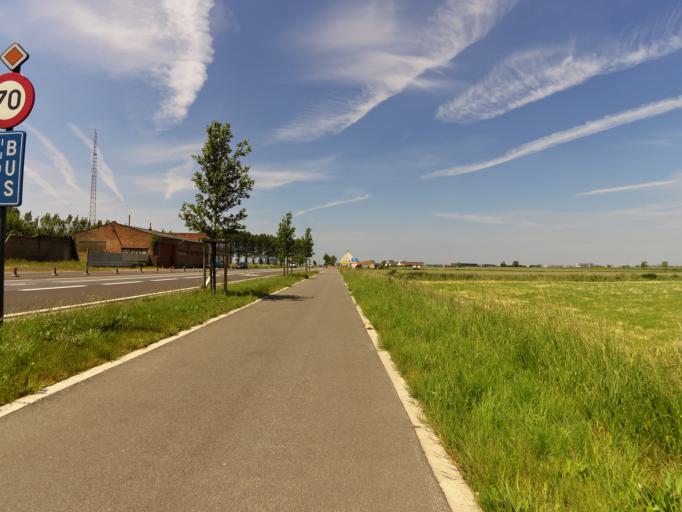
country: BE
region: Flanders
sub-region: Provincie West-Vlaanderen
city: Ostend
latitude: 51.1795
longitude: 2.9052
